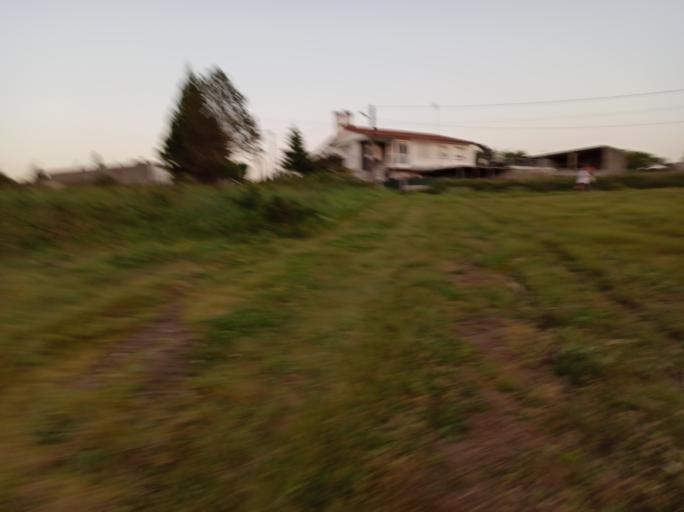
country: ES
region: Galicia
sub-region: Provincia da Coruna
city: Negreira
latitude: 42.9139
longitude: -8.7464
